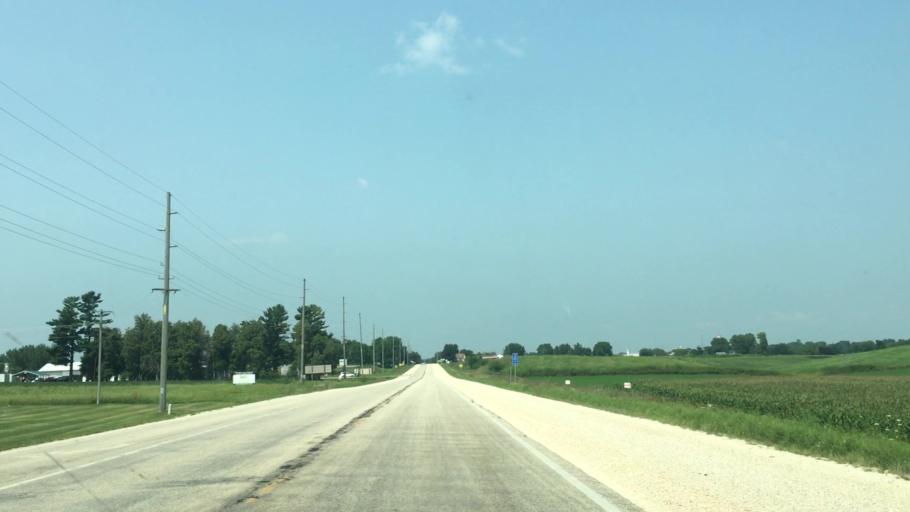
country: US
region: Iowa
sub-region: Fayette County
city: West Union
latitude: 42.9436
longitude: -91.8142
